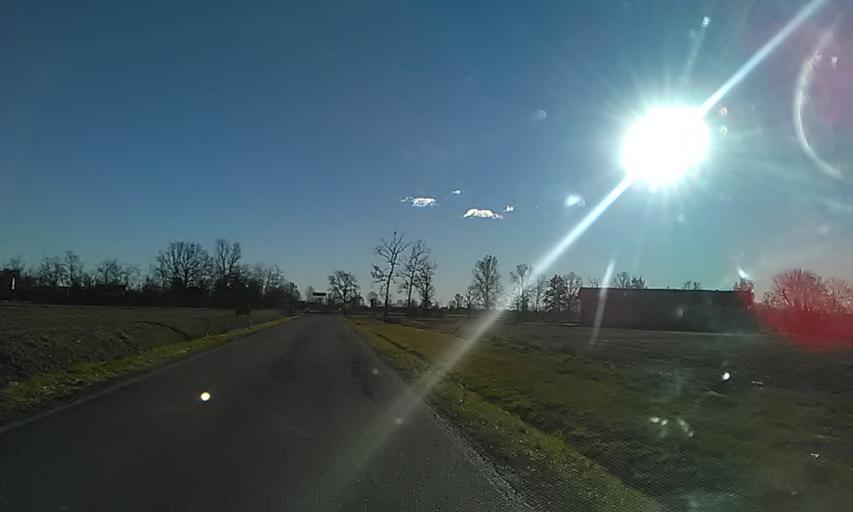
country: IT
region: Piedmont
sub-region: Provincia di Vercelli
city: Rovasenda
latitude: 45.5417
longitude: 8.2895
